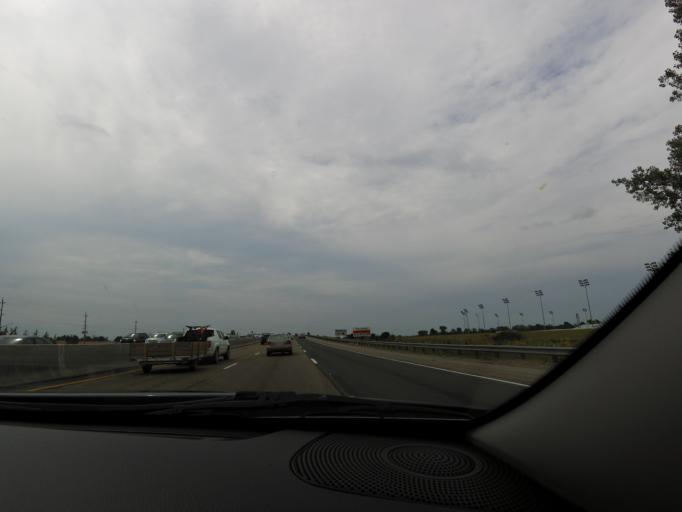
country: CA
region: Ontario
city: Innisfil
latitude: 44.2943
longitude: -79.6822
